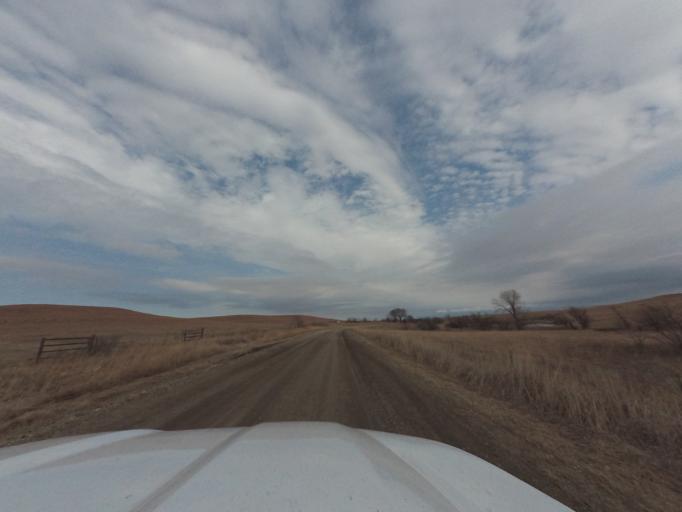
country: US
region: Kansas
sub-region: Chase County
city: Cottonwood Falls
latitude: 38.2500
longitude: -96.7305
